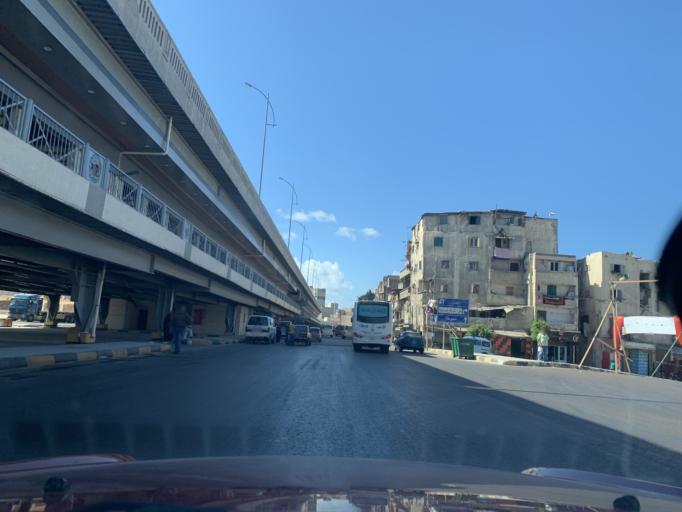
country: EG
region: Alexandria
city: Alexandria
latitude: 31.2240
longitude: 29.9838
